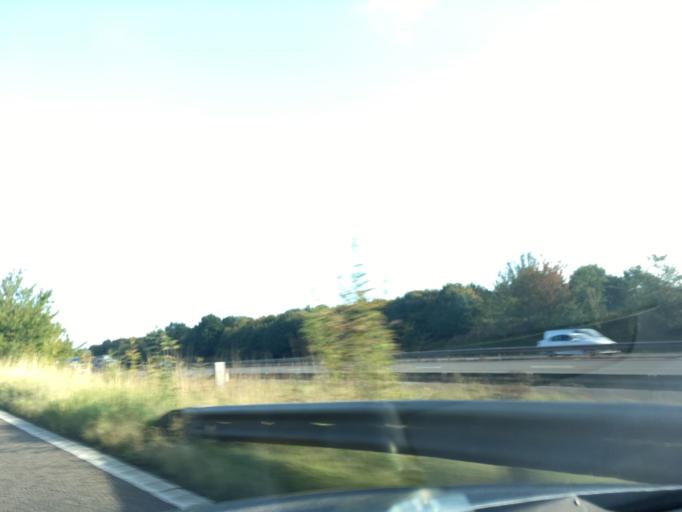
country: GB
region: England
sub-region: Oxfordshire
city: Banbury
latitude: 52.0693
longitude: -1.3116
